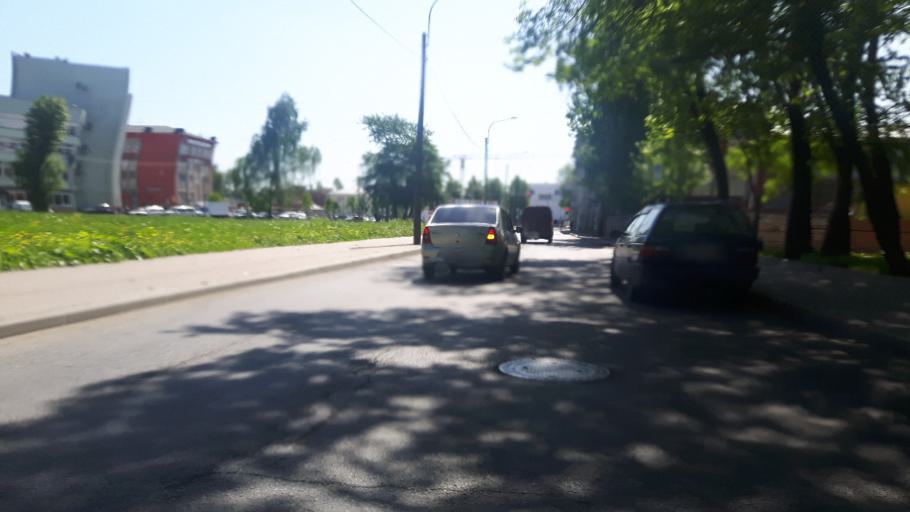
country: RU
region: St.-Petersburg
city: Admiralteisky
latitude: 59.8986
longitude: 30.2875
